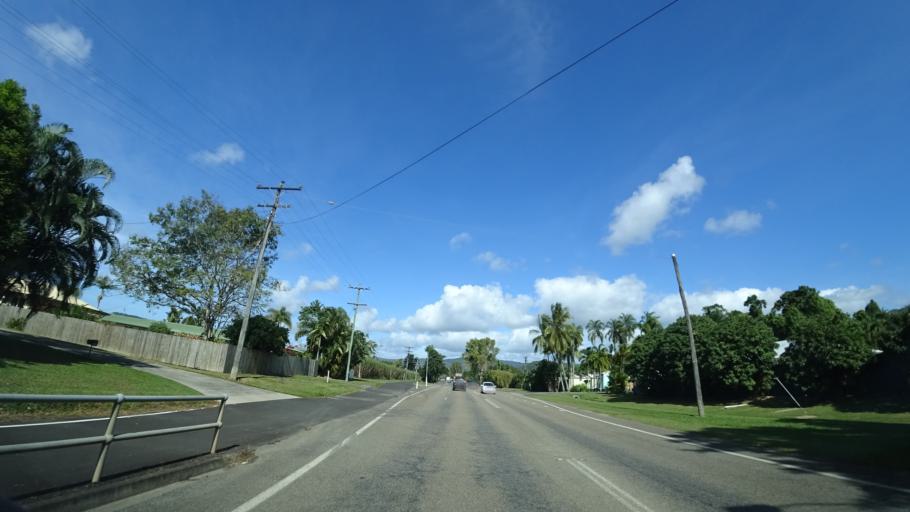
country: AU
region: Queensland
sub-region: Cairns
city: Port Douglas
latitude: -16.4695
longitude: 145.3731
